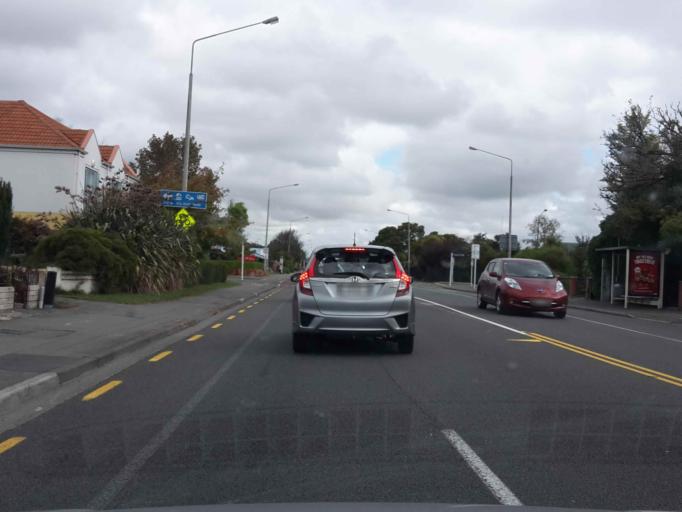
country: NZ
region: Canterbury
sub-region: Christchurch City
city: Christchurch
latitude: -43.4886
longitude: 172.6154
